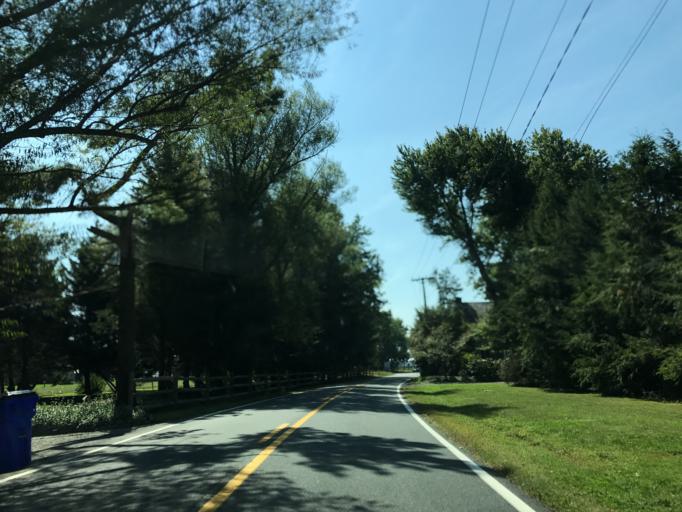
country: US
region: Delaware
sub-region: New Castle County
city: Middletown
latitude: 39.4956
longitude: -75.8084
